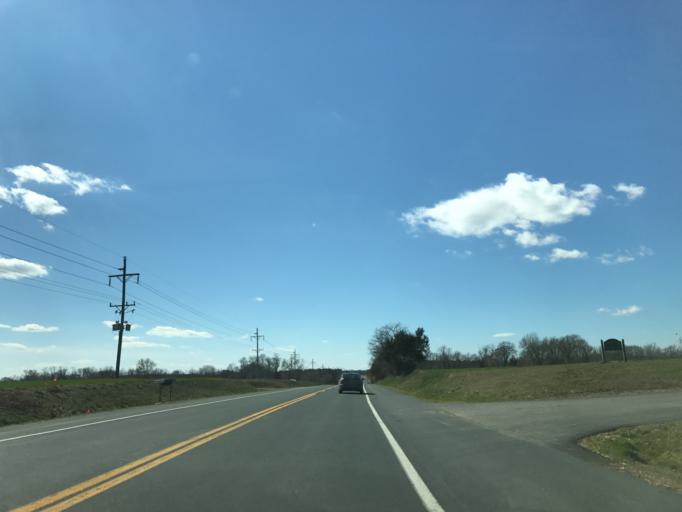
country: US
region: Maryland
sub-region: Queen Anne's County
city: Kingstown
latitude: 39.2583
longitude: -75.9334
